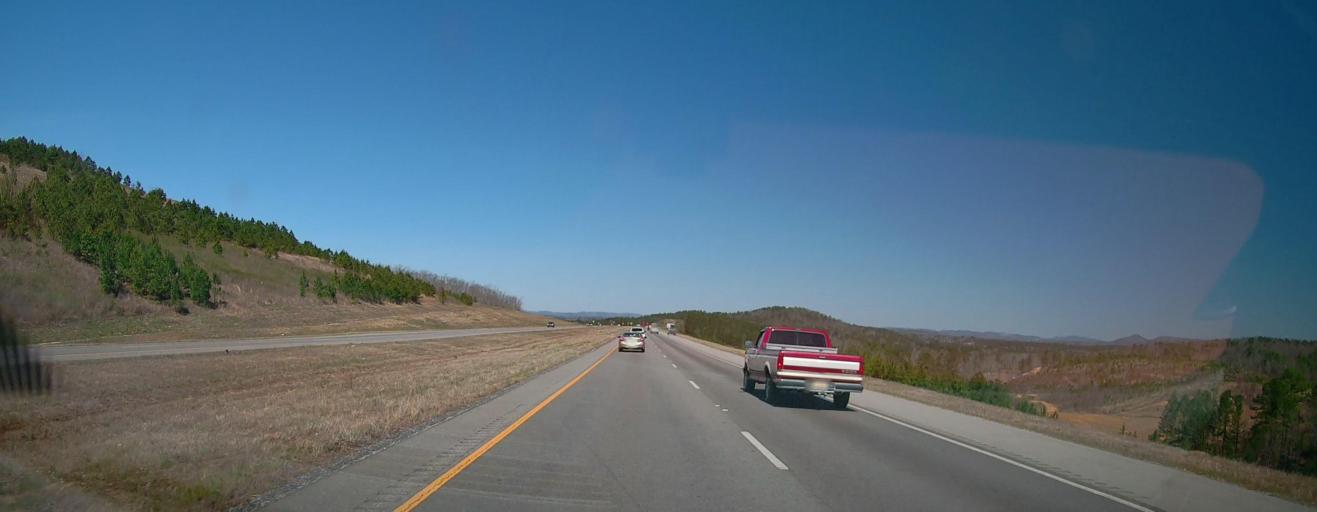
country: US
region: Alabama
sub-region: Calhoun County
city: Saks
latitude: 33.6928
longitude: -85.8060
